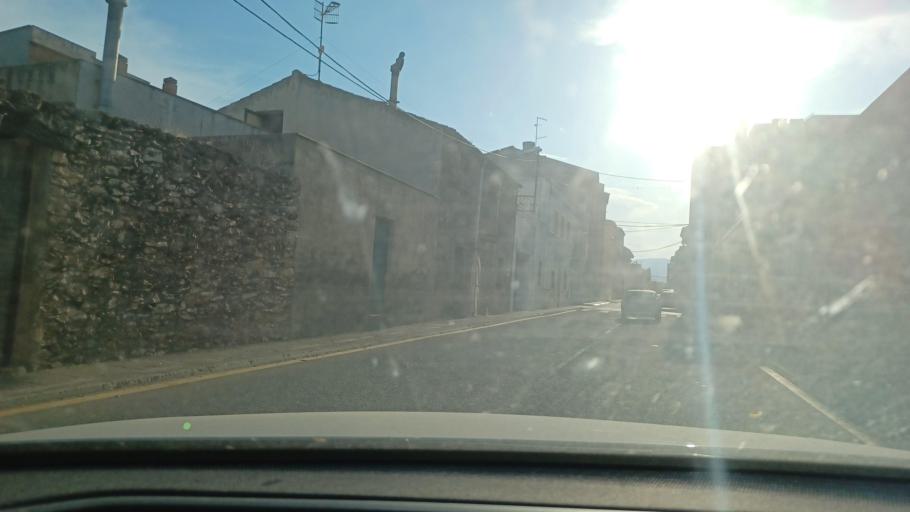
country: ES
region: Catalonia
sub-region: Provincia de Tarragona
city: Santa Barbara
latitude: 40.7127
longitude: 0.4964
